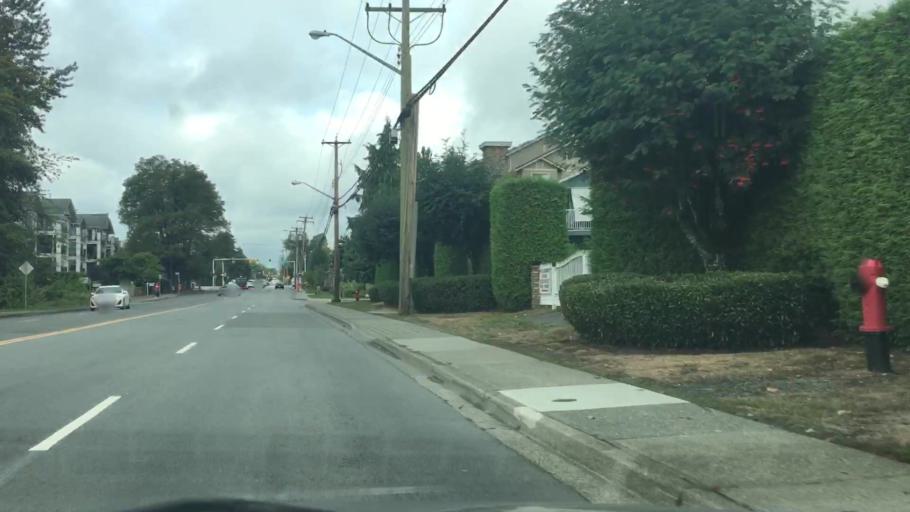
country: CA
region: British Columbia
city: Langley
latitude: 49.1046
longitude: -122.6397
